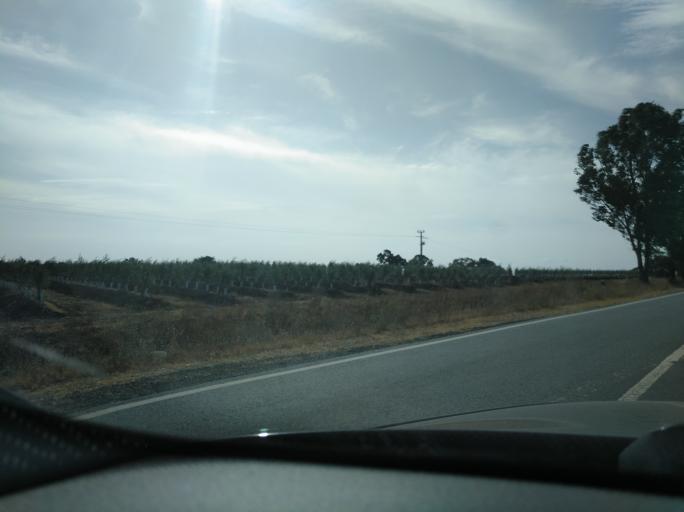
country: PT
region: Beja
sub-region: Beja
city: Ferreira do Alentejo
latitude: 38.0501
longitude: -7.9618
